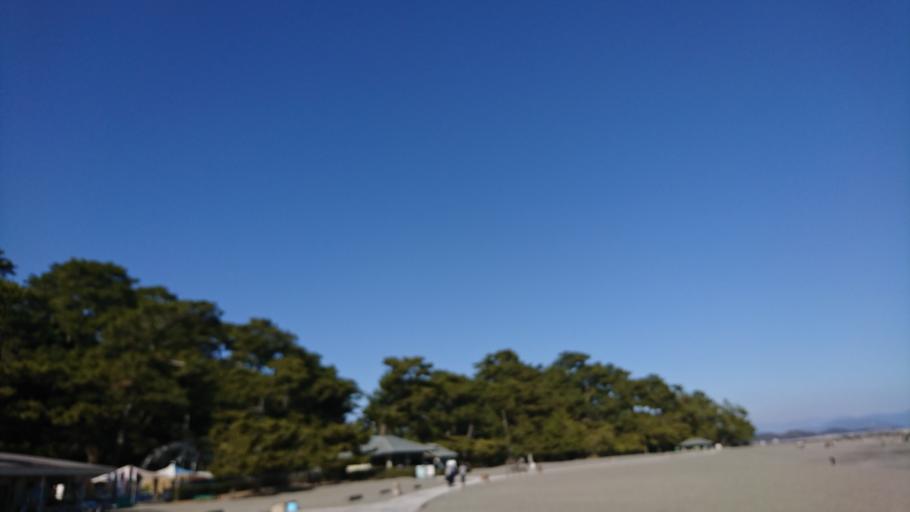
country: JP
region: Kochi
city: Kochi-shi
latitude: 33.4969
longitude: 133.5740
